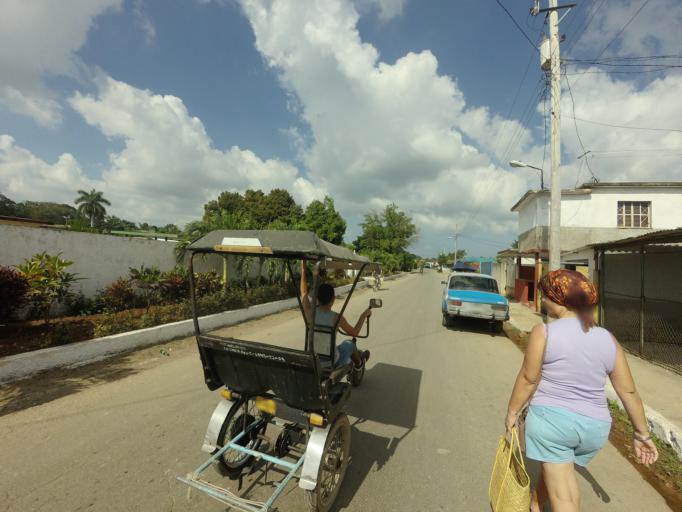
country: CU
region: Artemisa
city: Bauta
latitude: 22.9828
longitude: -82.5512
